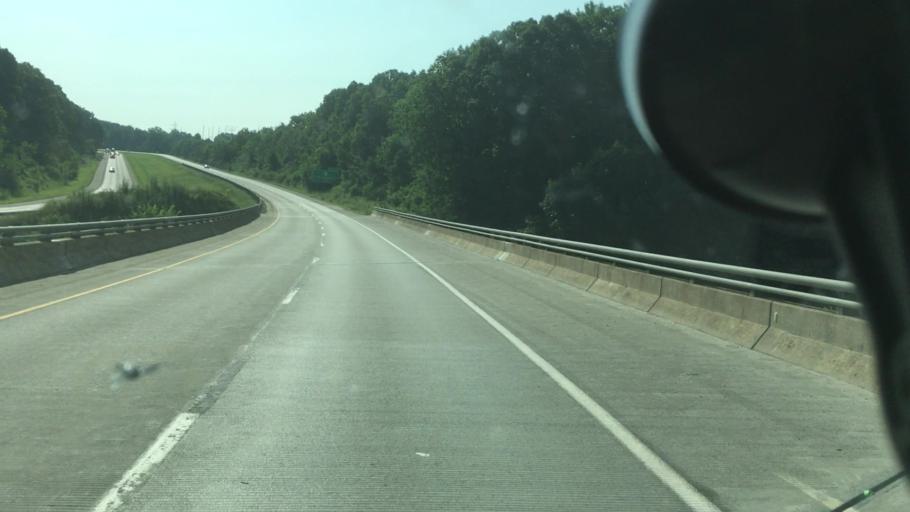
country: US
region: Pennsylvania
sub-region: Lawrence County
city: New Castle
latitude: 40.9686
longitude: -80.3377
